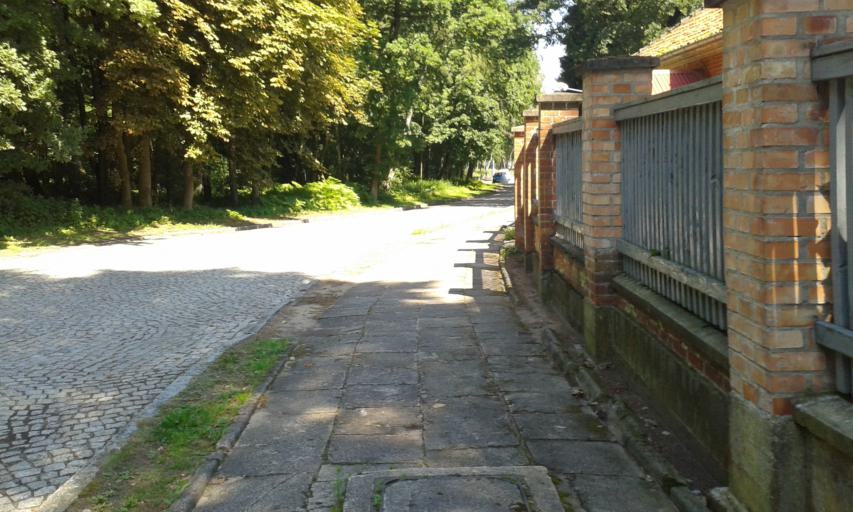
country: PL
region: Pomeranian Voivodeship
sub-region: Powiat nowodworski
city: Sztutowo
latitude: 54.3272
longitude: 19.1532
